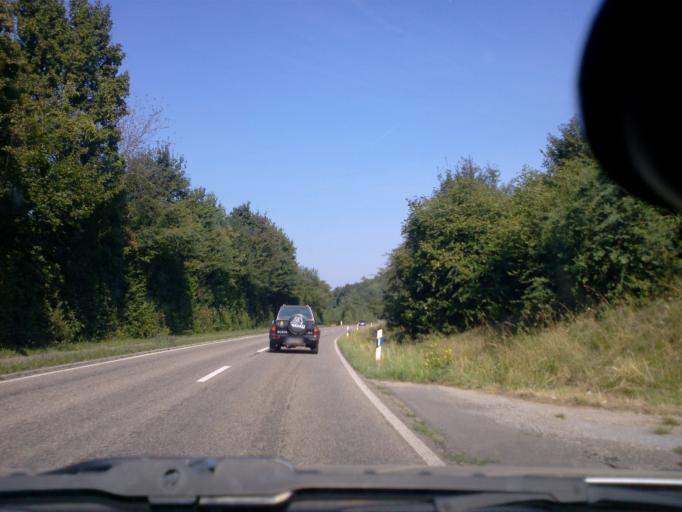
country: DE
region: Baden-Wuerttemberg
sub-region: Karlsruhe Region
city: Joehlingen
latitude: 49.0794
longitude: 8.5707
